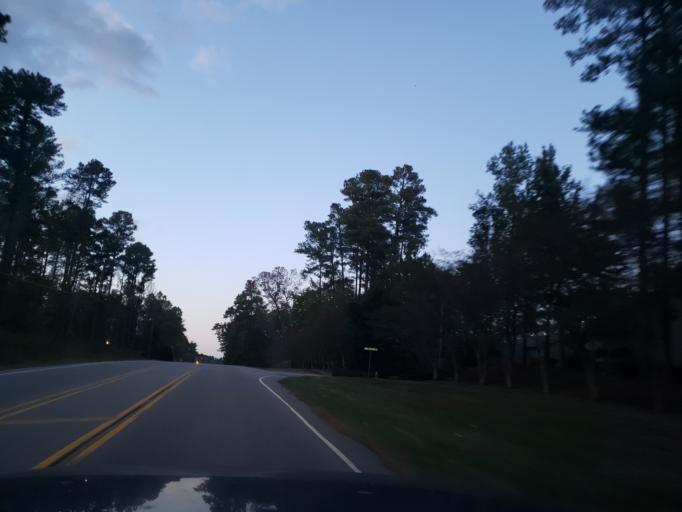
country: US
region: North Carolina
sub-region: Orange County
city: Chapel Hill
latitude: 35.8954
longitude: -78.9586
